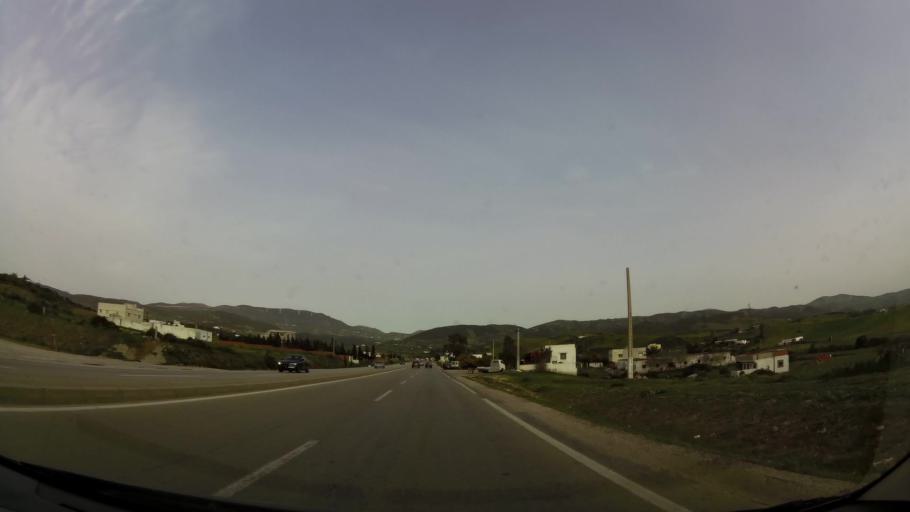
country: MA
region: Tanger-Tetouan
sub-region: Tanger-Assilah
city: Dar Chaoui
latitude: 35.5692
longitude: -5.6222
